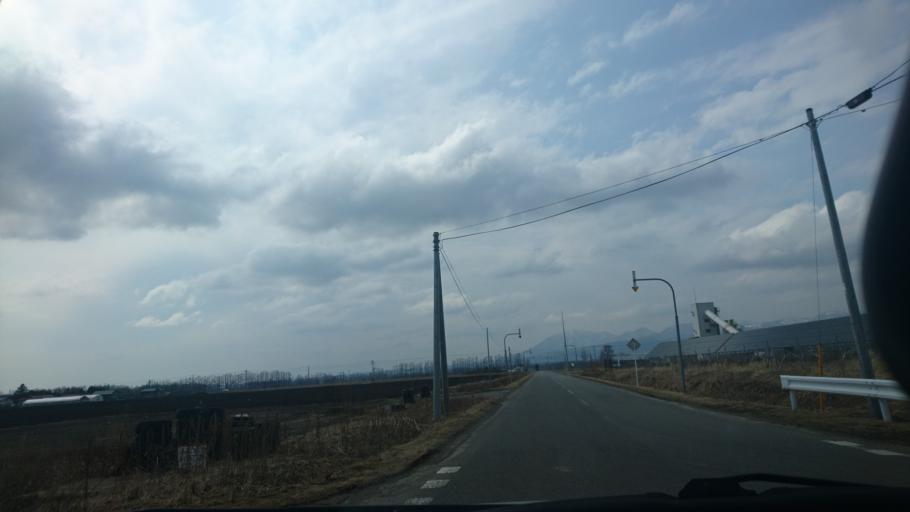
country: JP
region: Hokkaido
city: Otofuke
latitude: 43.2159
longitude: 143.2843
